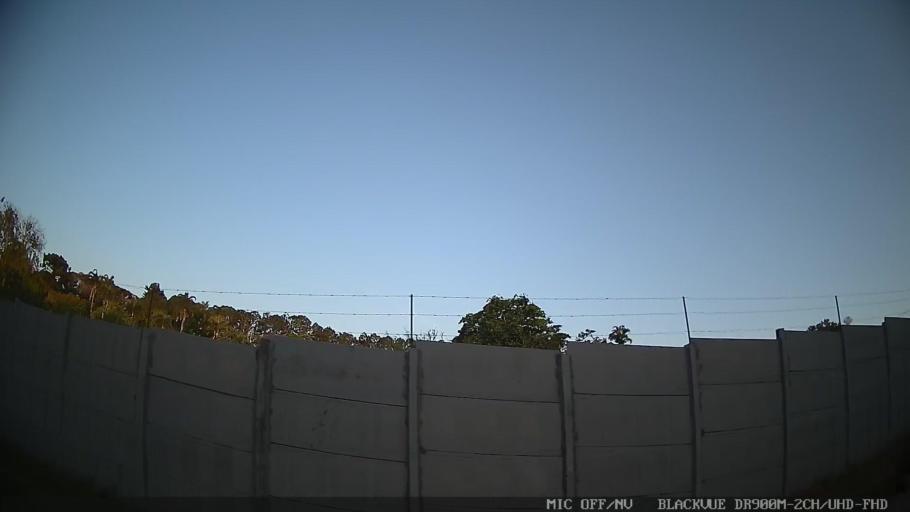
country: BR
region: Sao Paulo
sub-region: Itupeva
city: Itupeva
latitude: -23.2263
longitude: -47.0859
